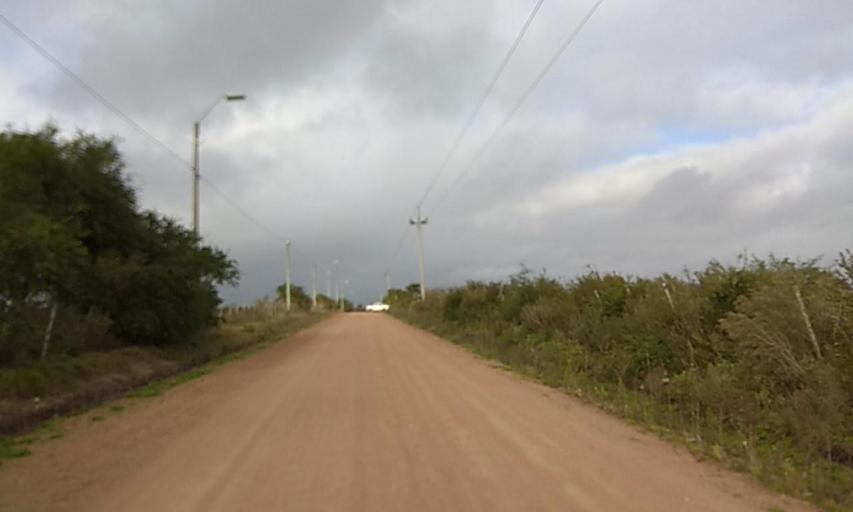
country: UY
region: Florida
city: Florida
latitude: -34.0619
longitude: -56.2170
